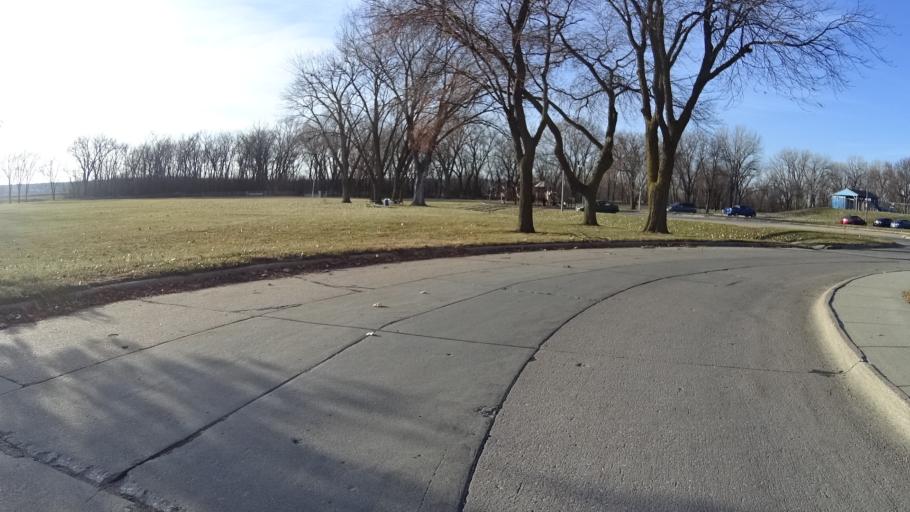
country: US
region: Nebraska
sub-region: Sarpy County
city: La Vista
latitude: 41.1847
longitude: -95.9985
